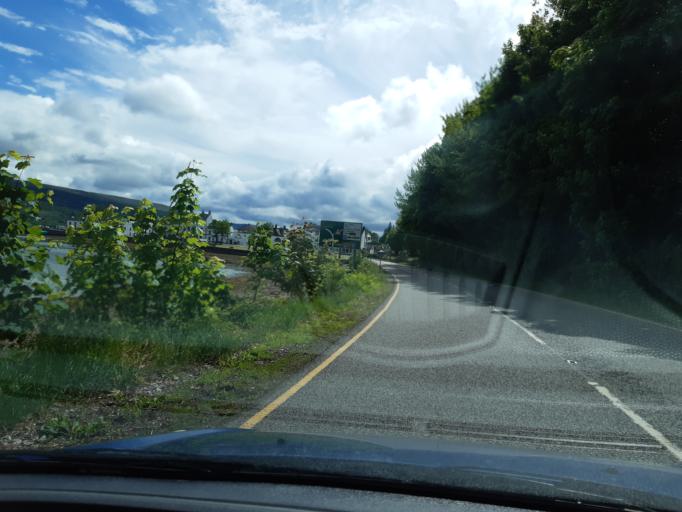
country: GB
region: Scotland
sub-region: Argyll and Bute
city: Garelochhead
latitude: 56.2340
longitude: -5.0731
